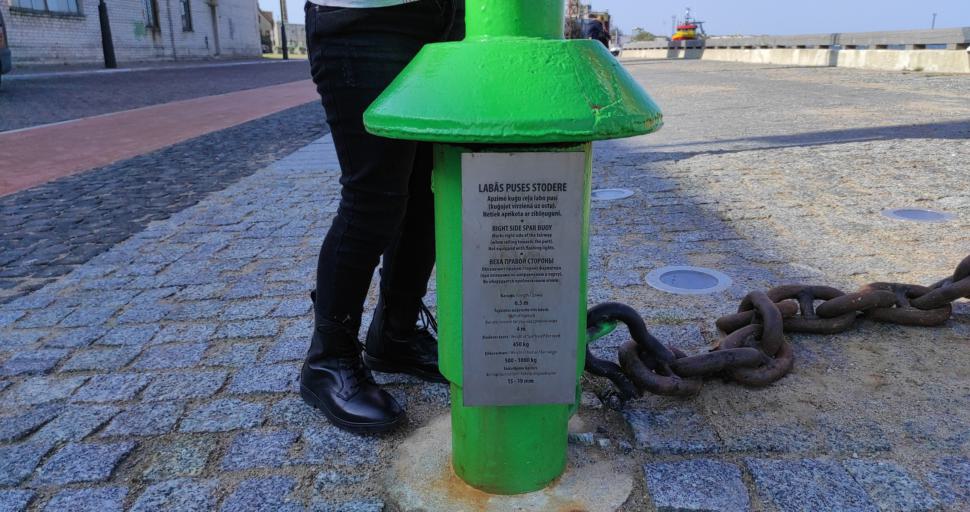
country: LV
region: Ventspils
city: Ventspils
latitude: 57.3944
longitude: 21.5453
